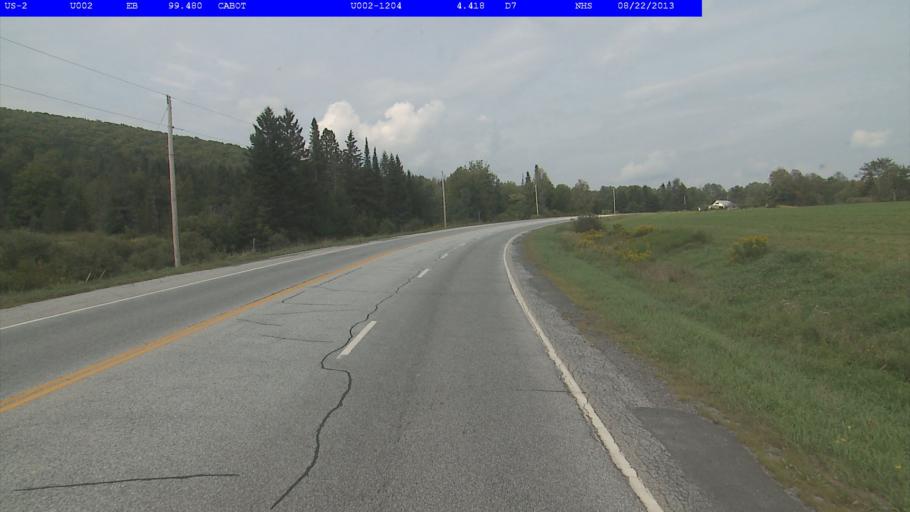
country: US
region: Vermont
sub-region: Caledonia County
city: Hardwick
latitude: 44.3880
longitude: -72.2546
